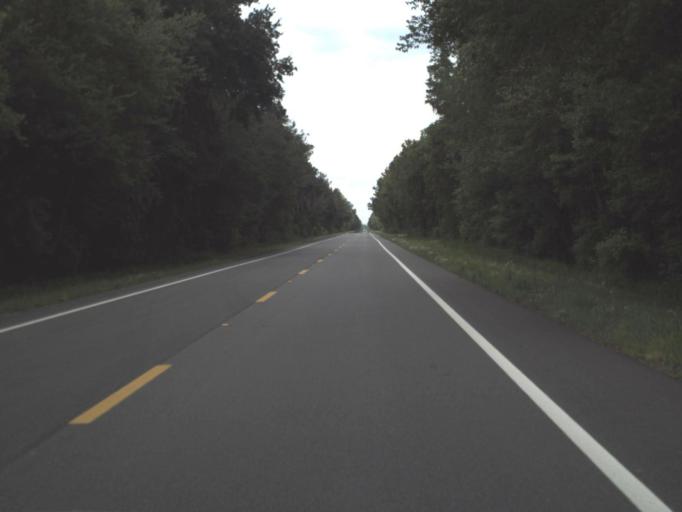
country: US
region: Florida
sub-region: Hamilton County
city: Jasper
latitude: 30.5590
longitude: -82.6807
